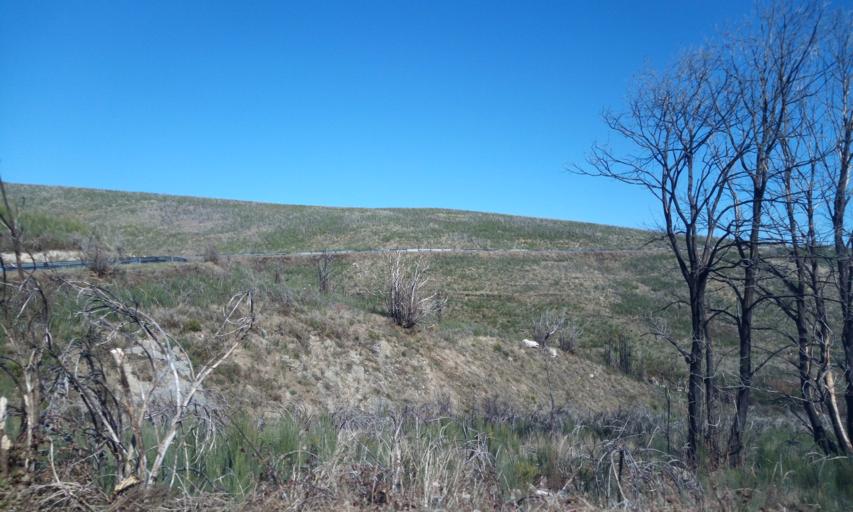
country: PT
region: Guarda
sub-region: Manteigas
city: Manteigas
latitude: 40.4699
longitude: -7.5205
